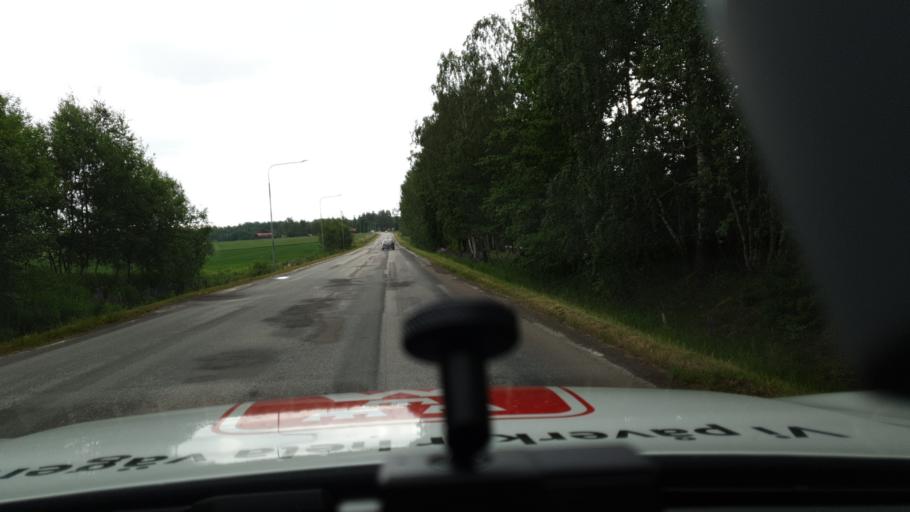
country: SE
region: Vaestra Goetaland
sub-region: Tibro Kommun
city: Tibro
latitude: 58.4159
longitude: 14.1931
